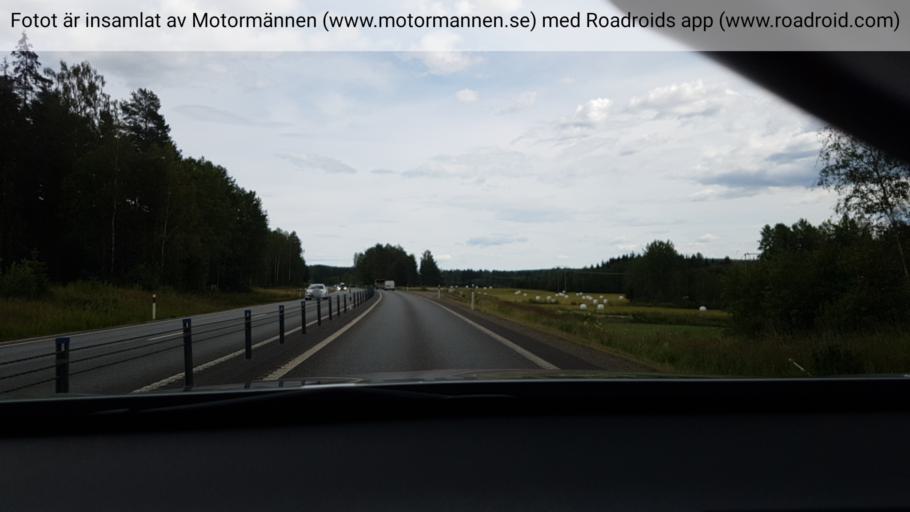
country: SE
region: Vaermland
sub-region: Arvika Kommun
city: Arvika
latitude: 59.6555
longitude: 12.6508
